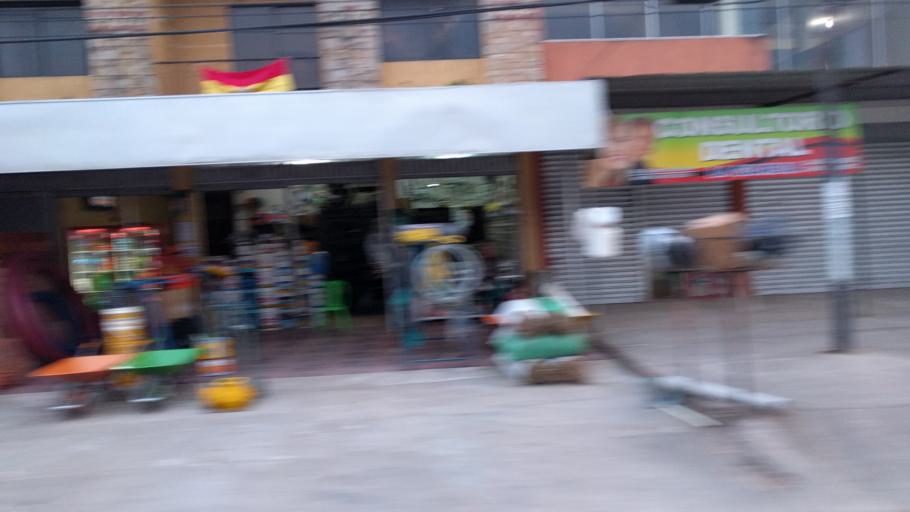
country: BO
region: Santa Cruz
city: Santa Rita
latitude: -17.8918
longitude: -63.3215
